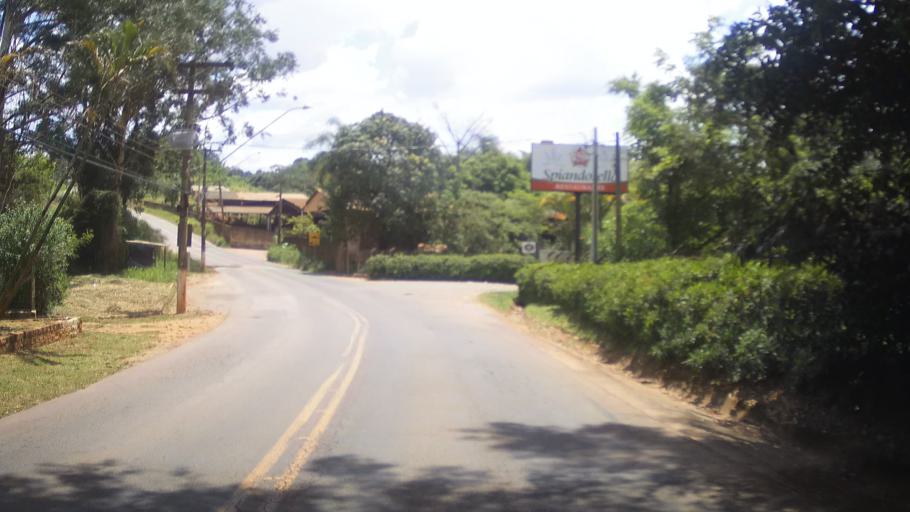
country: BR
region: Sao Paulo
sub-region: Varzea Paulista
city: Varzea Paulista
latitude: -23.1490
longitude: -46.8213
